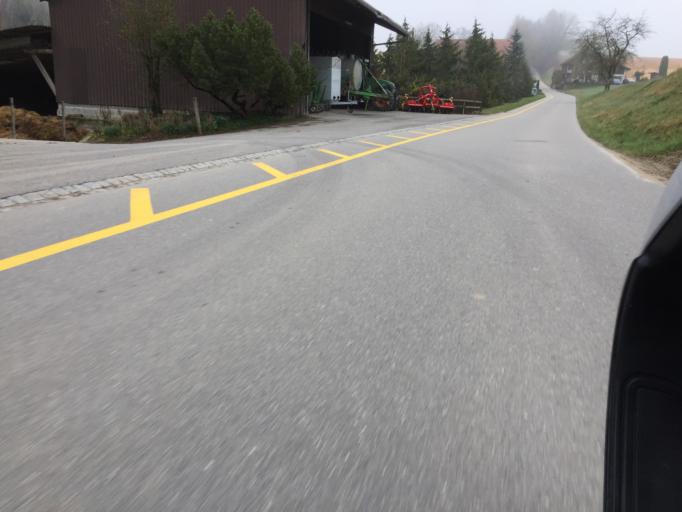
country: CH
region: Bern
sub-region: Seeland District
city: Grossaffoltern
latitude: 47.1025
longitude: 7.3624
